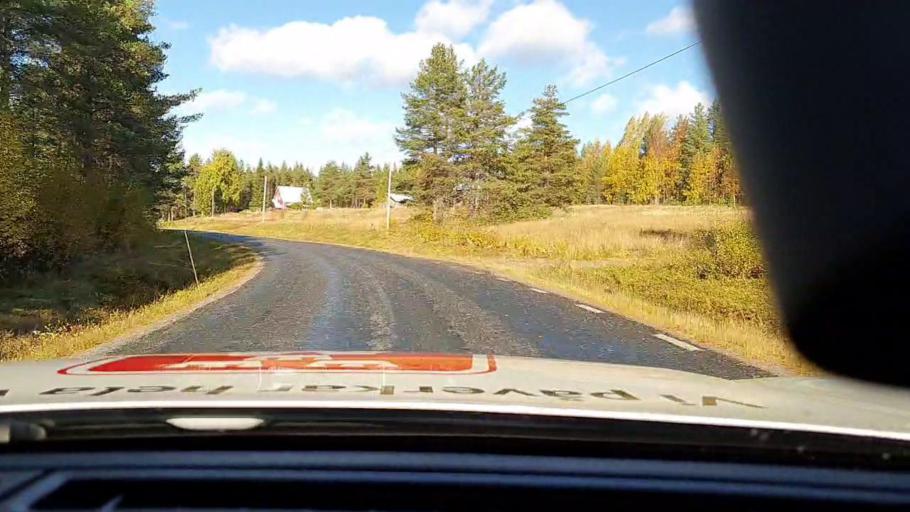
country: SE
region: Vaesterbotten
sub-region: Skelleftea Kommun
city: Langsele
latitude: 65.0139
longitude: 20.0797
